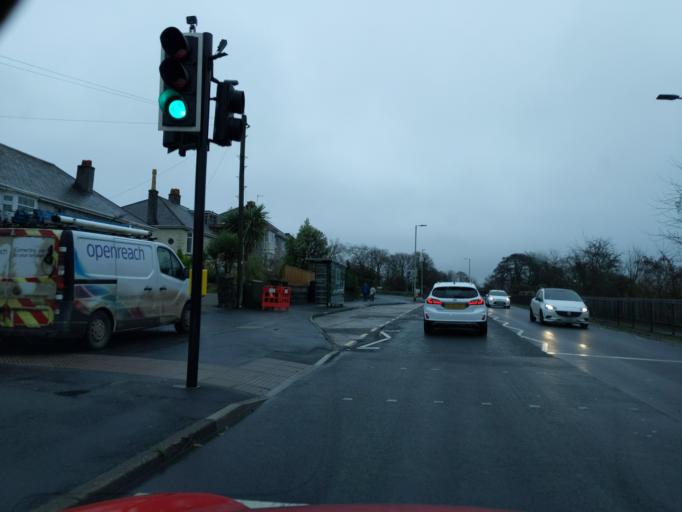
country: GB
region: England
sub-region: Devon
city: Plympton
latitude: 50.3896
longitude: -4.0648
